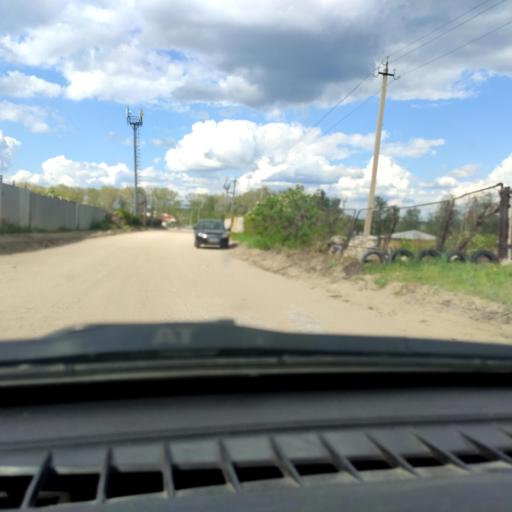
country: RU
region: Samara
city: Zhigulevsk
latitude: 53.4545
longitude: 49.5353
